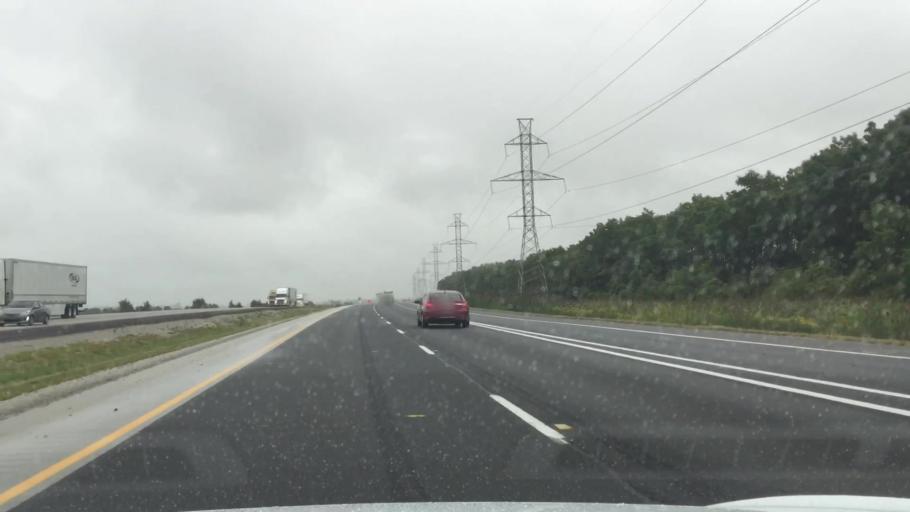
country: CA
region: Ontario
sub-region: Lambton County
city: Walpole Island
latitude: 42.3526
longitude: -82.1807
